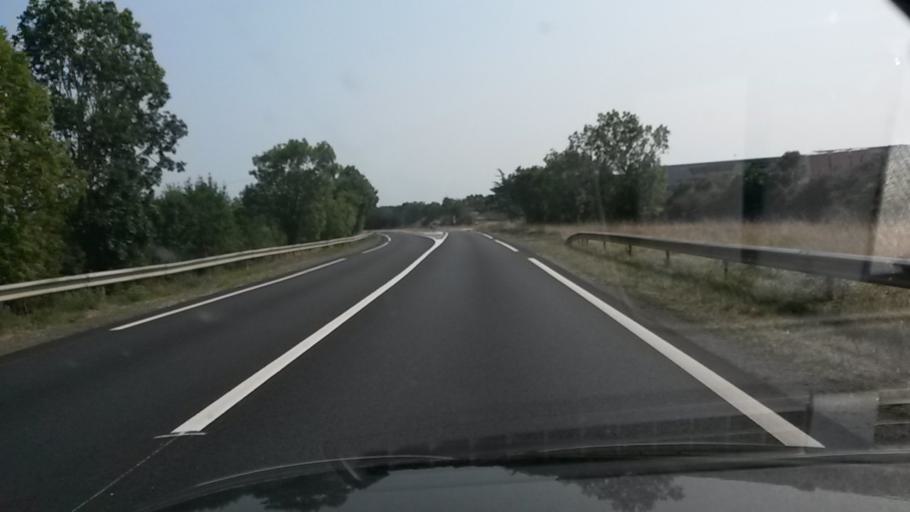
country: FR
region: Pays de la Loire
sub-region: Departement de la Loire-Atlantique
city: Ancenis
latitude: 47.3787
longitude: -1.1720
